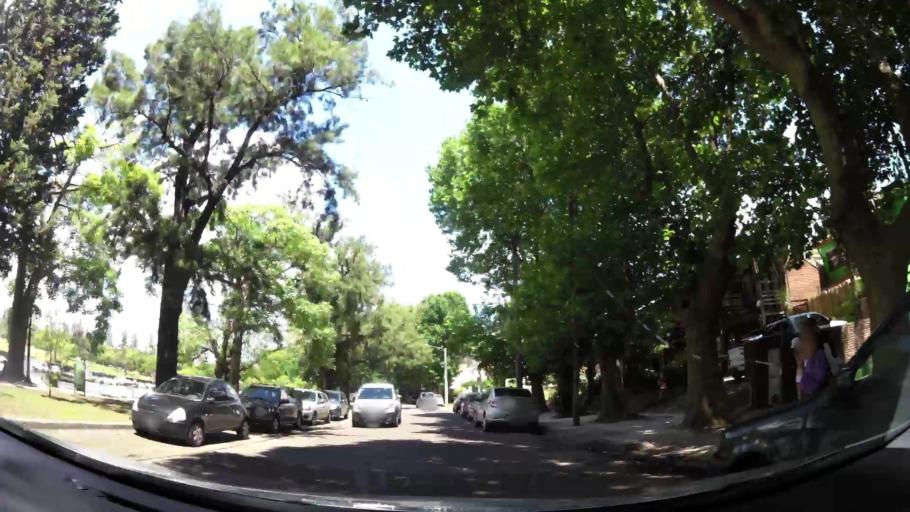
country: AR
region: Buenos Aires
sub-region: Partido de Tigre
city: Tigre
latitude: -34.4229
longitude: -58.5836
